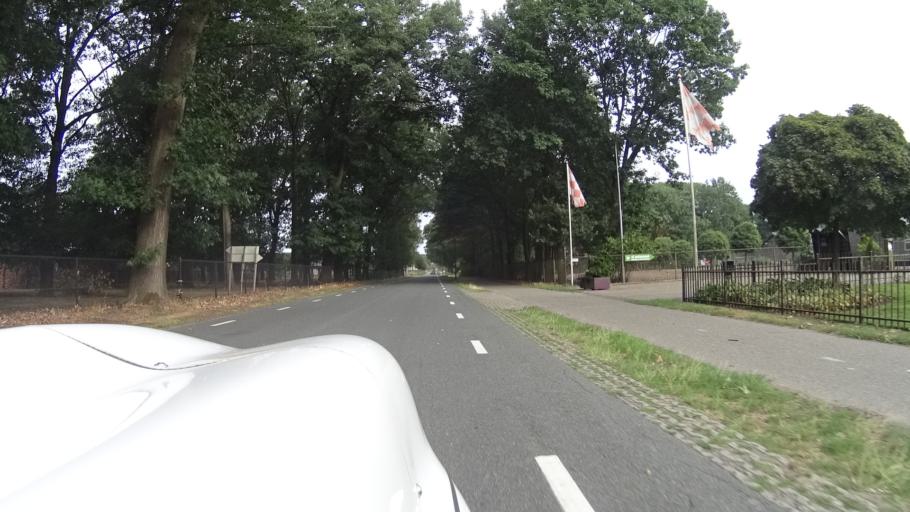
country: NL
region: North Brabant
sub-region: Gemeente Boxmeer
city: Overloon
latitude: 51.5930
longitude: 5.9256
